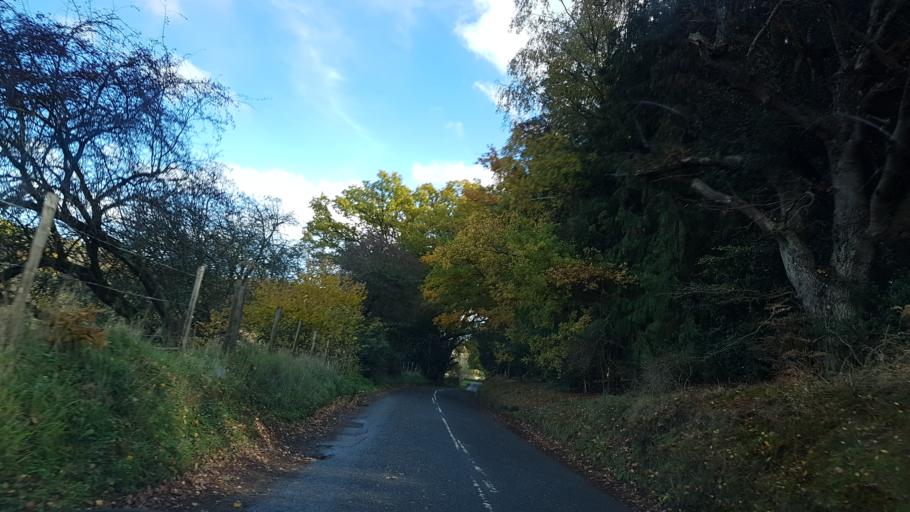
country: GB
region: England
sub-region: Surrey
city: Seale
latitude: 51.2222
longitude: -0.7060
